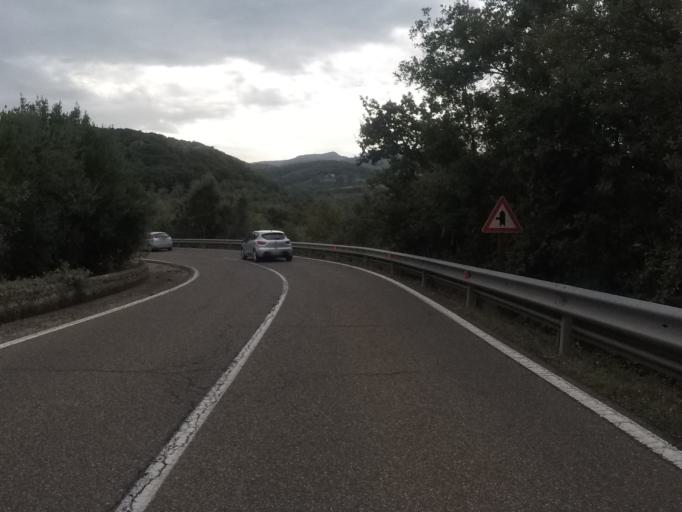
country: IT
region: Sardinia
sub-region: Provincia di Oristano
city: Sennariolo
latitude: 40.2129
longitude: 8.5594
